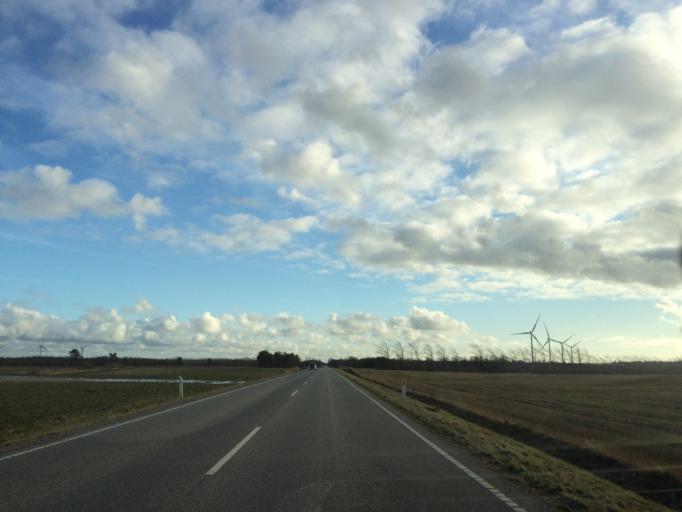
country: DK
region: Central Jutland
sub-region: Holstebro Kommune
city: Ulfborg
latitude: 56.3928
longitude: 8.3211
